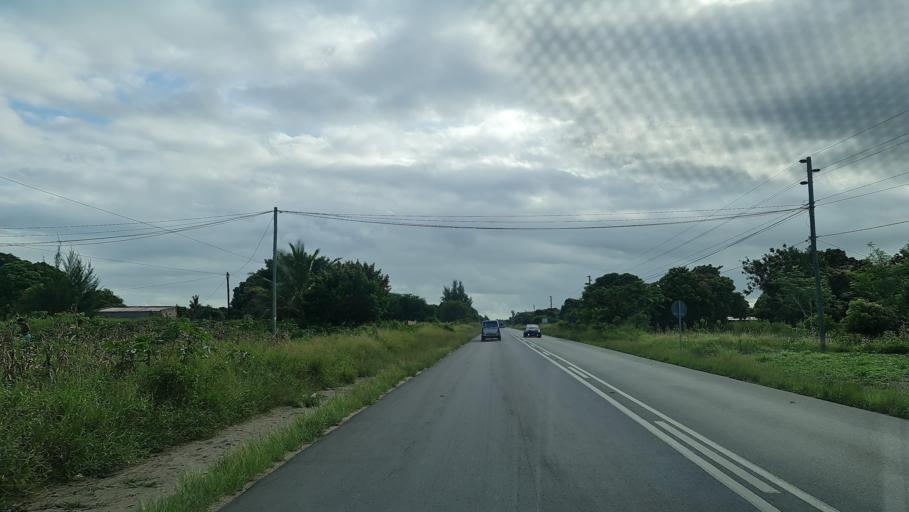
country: MZ
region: Maputo
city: Manhica
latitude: -25.4175
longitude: 32.7333
